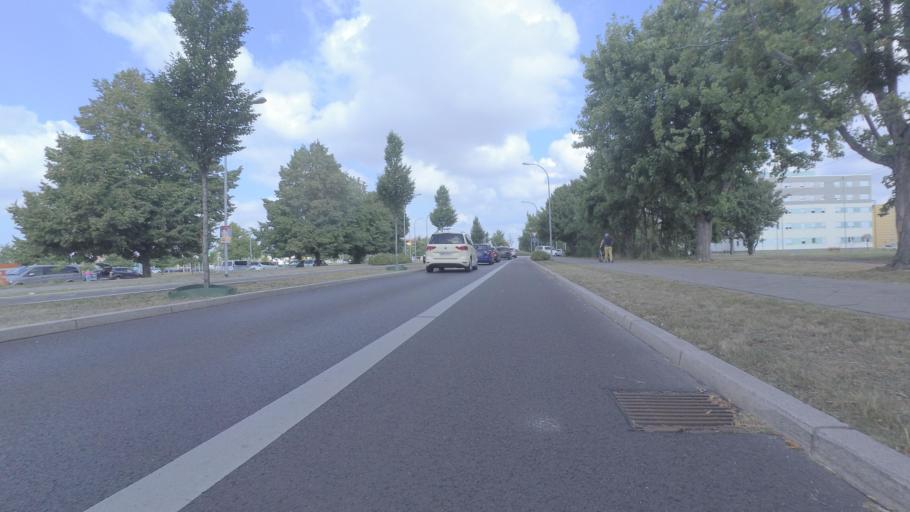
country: DE
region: Brandenburg
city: Neuruppin
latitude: 52.9165
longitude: 12.7915
